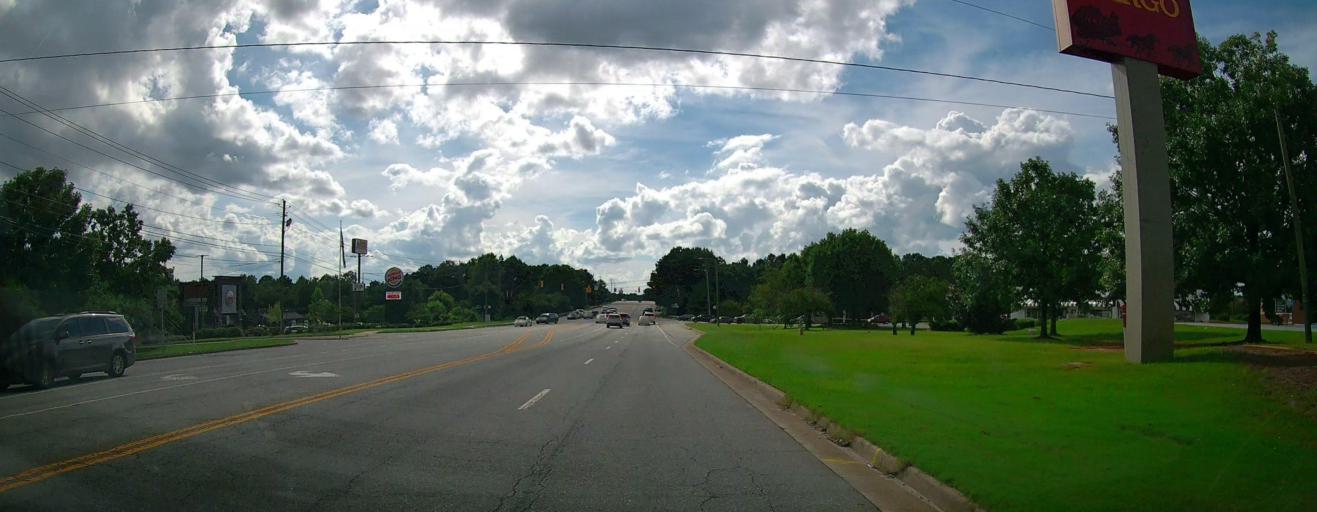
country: US
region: Alabama
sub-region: Russell County
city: Phenix City
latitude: 32.5323
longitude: -84.9690
